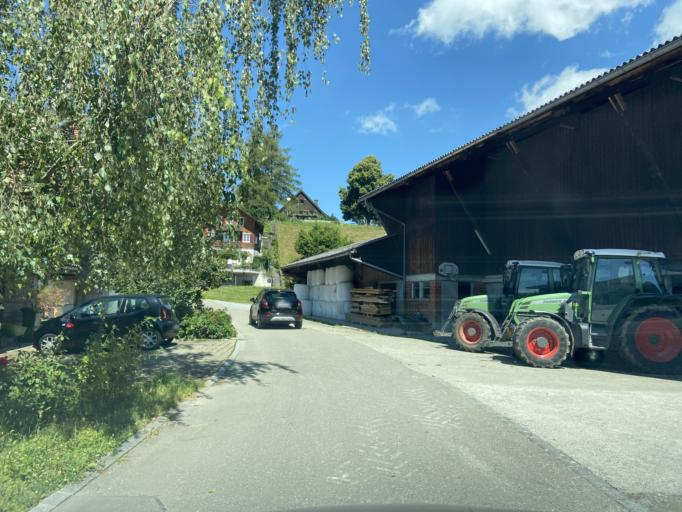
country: CH
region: Zurich
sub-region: Bezirk Meilen
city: Uerikon
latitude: 47.2462
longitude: 8.7573
